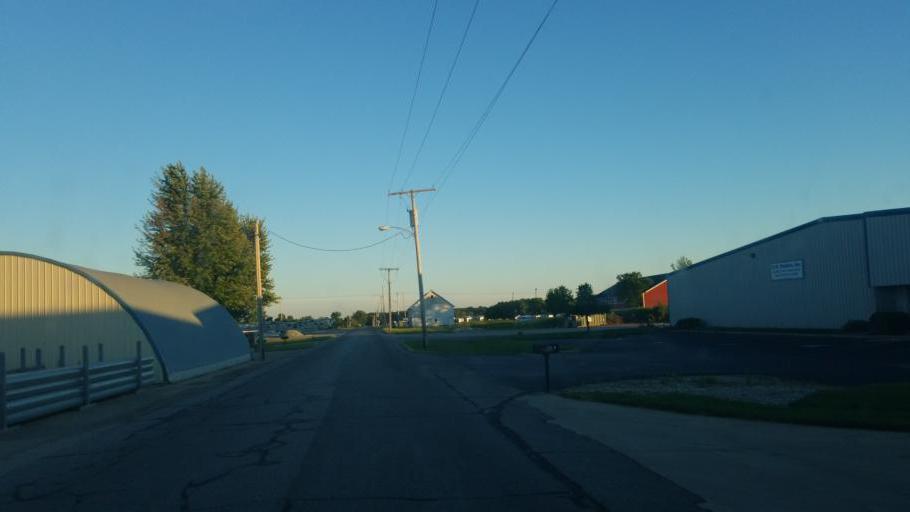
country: US
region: Indiana
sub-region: Elkhart County
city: Nappanee
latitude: 41.4456
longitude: -86.0304
